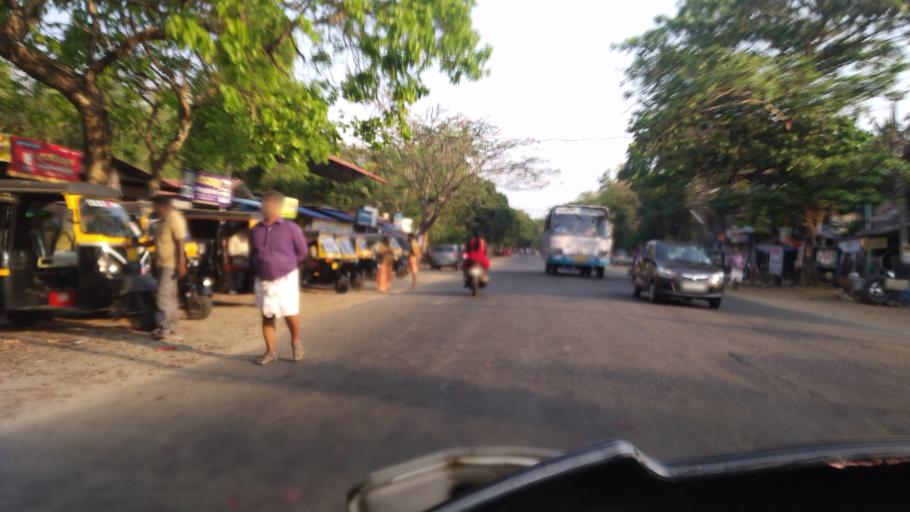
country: IN
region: Kerala
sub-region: Thrissur District
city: Thanniyam
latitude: 10.4403
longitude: 76.0949
